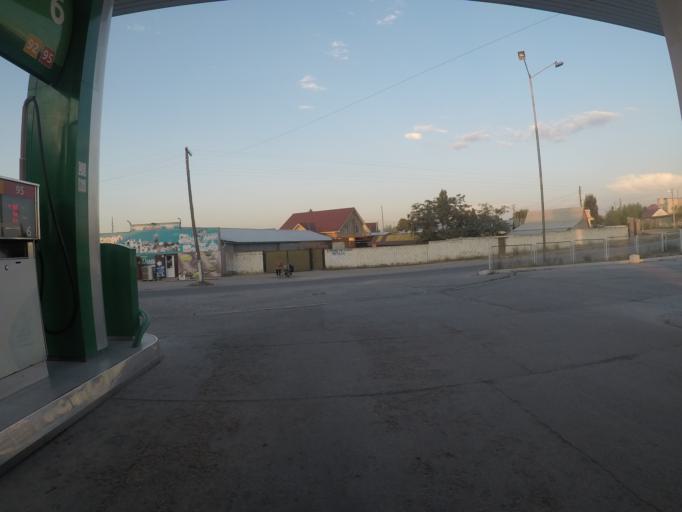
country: KG
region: Chuy
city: Lebedinovka
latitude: 42.8014
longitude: 74.6496
